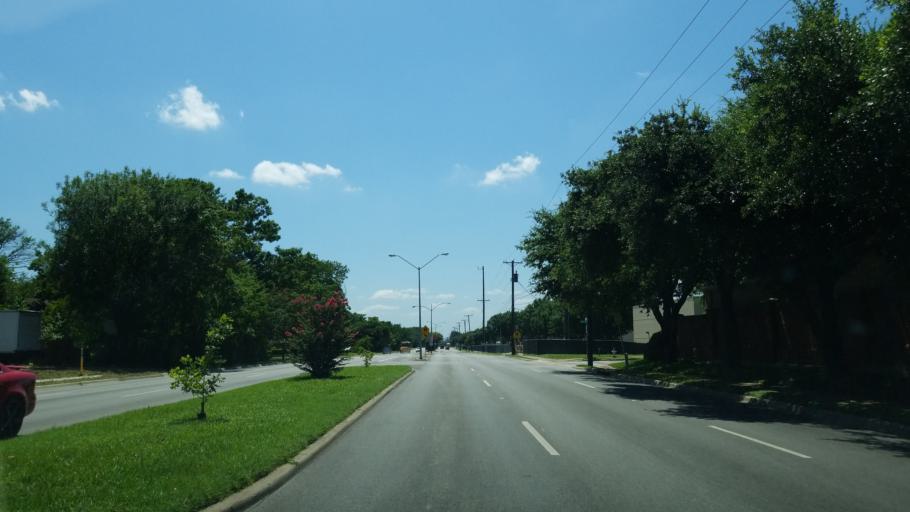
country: US
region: Texas
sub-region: Dallas County
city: University Park
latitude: 32.8804
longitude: -96.8428
